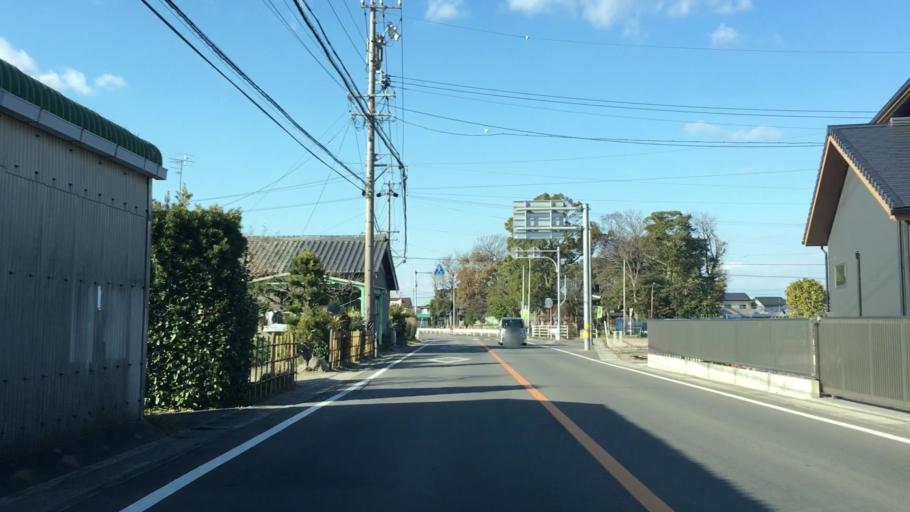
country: JP
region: Aichi
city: Nishio
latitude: 34.8501
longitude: 137.0593
